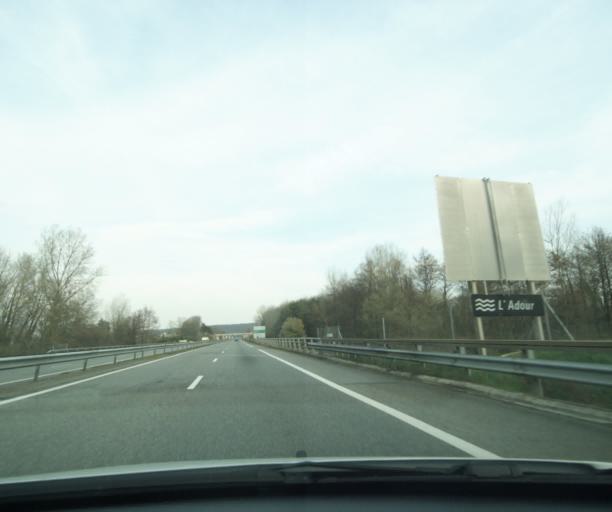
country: FR
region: Midi-Pyrenees
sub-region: Departement des Hautes-Pyrenees
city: Soues
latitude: 43.2151
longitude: 0.0915
